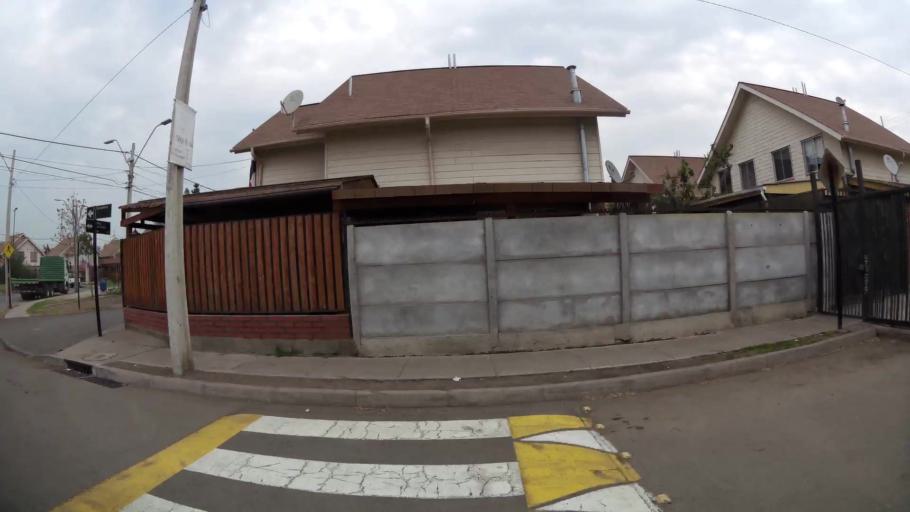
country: CL
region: Santiago Metropolitan
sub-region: Provincia de Chacabuco
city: Chicureo Abajo
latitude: -33.2019
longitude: -70.6814
